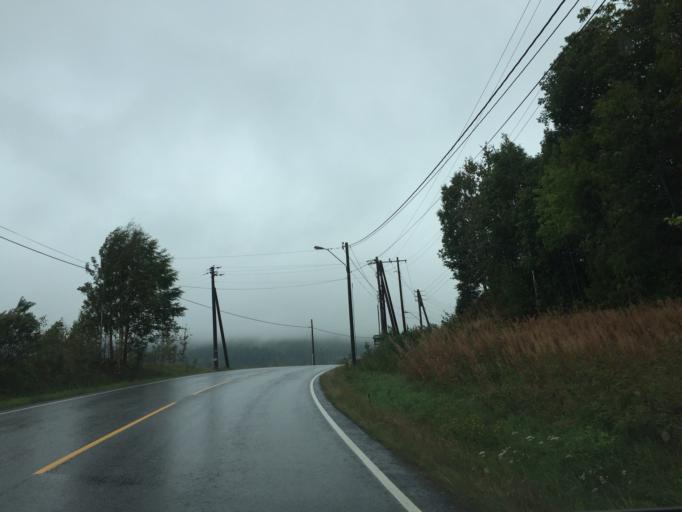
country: NO
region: Akershus
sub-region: Baerum
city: Lysaker
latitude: 59.9792
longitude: 10.6219
